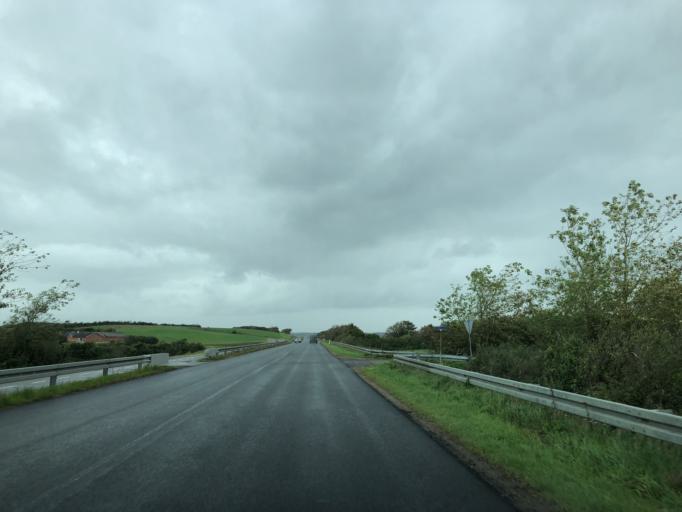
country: DK
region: Central Jutland
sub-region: Struer Kommune
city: Struer
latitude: 56.5476
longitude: 8.5593
